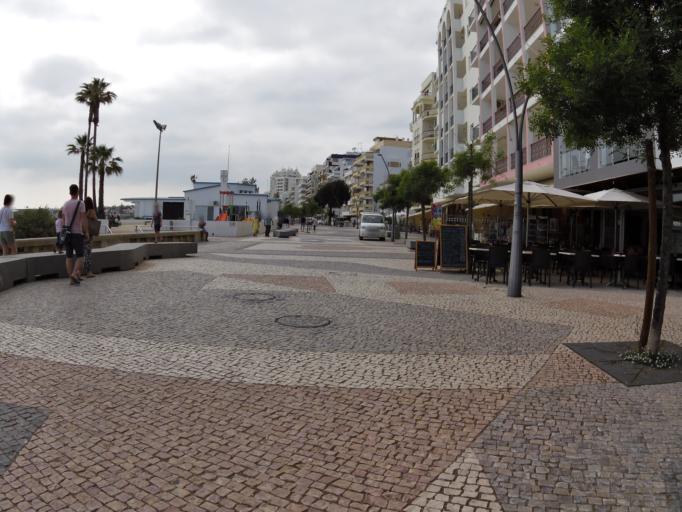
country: PT
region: Faro
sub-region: Silves
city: Armacao de Pera
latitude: 37.1014
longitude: -8.3626
